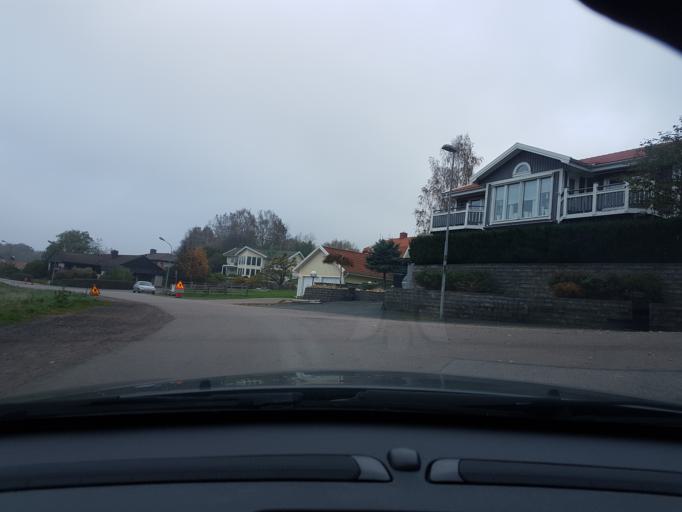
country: SE
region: Vaestra Goetaland
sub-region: Ale Kommun
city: Surte
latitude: 57.8223
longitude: 12.0230
